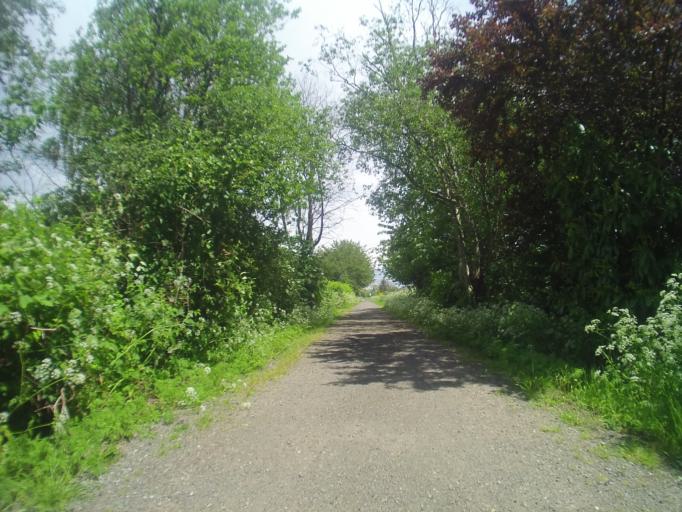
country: CA
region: British Columbia
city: Richmond
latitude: 49.1944
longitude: -123.1101
